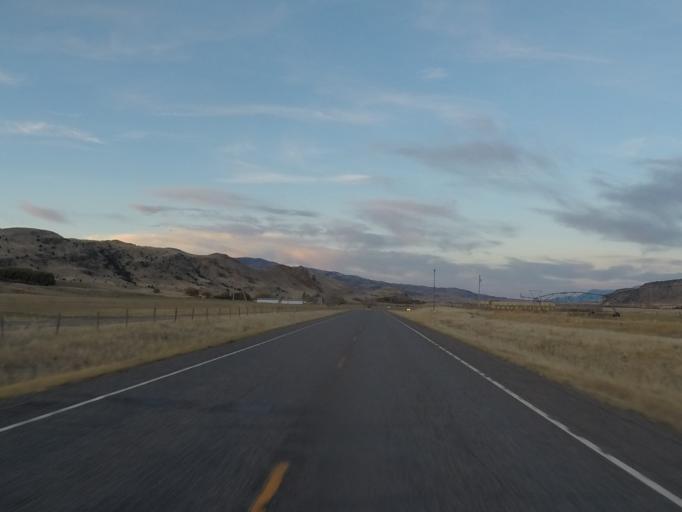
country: US
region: Montana
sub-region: Gallatin County
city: Bozeman
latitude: 45.2710
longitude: -110.8602
